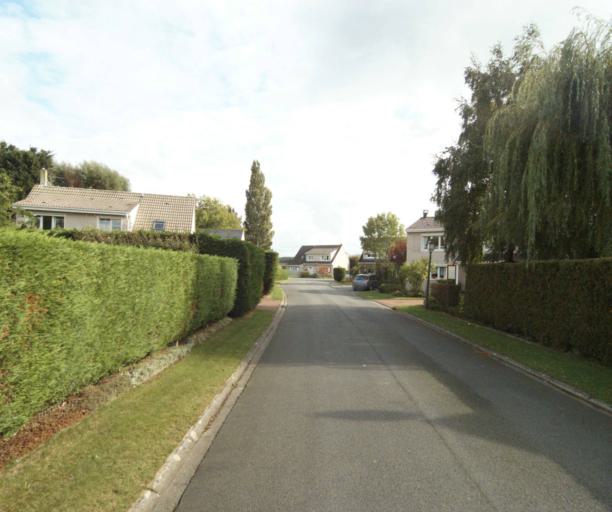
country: FR
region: Nord-Pas-de-Calais
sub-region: Departement du Nord
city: Premesques
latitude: 50.6598
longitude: 2.9314
